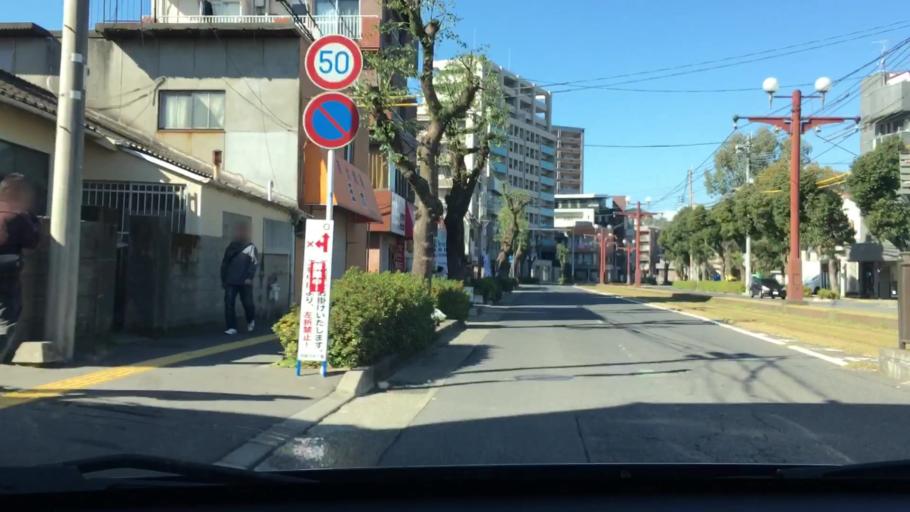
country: JP
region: Kagoshima
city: Kagoshima-shi
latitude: 31.5650
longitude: 130.5451
